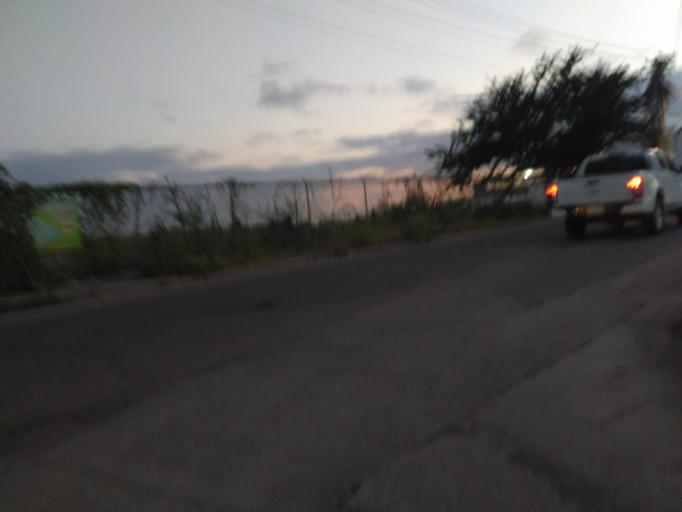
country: MX
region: Sinaloa
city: Culiacan
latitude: 24.7816
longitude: -107.3906
